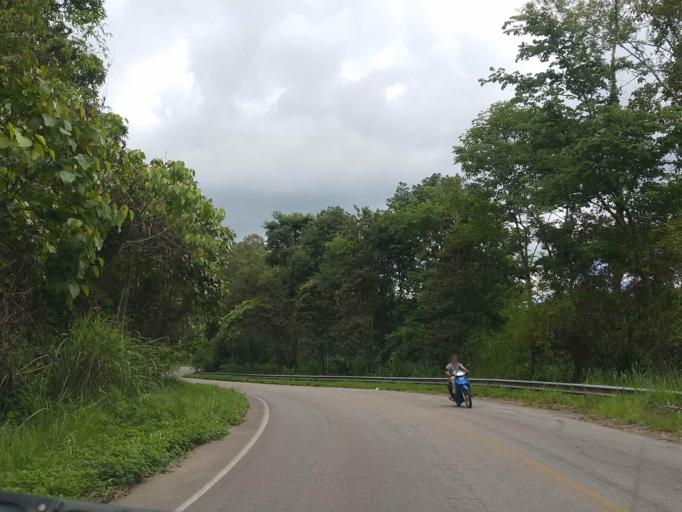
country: TH
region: Chiang Mai
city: Samoeng
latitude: 18.8092
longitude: 98.8183
